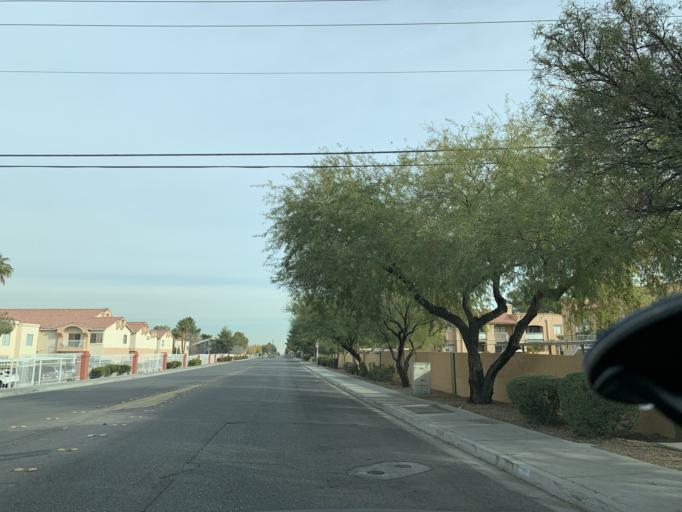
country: US
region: Nevada
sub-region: Clark County
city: Spring Valley
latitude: 36.0963
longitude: -115.2241
